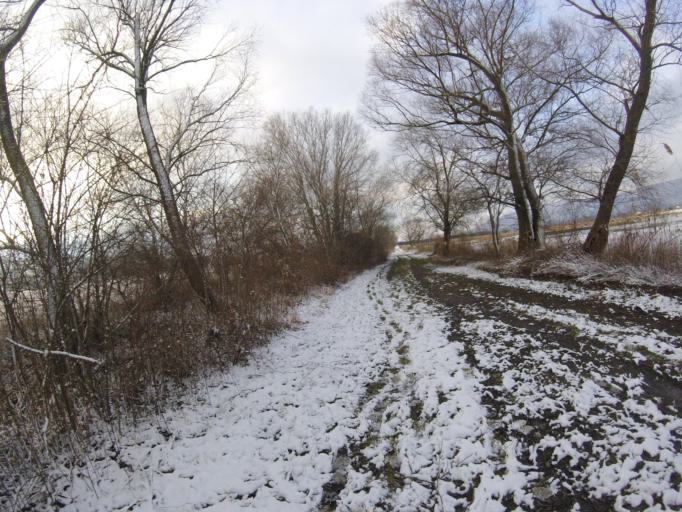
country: HU
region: Komarom-Esztergom
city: Esztergom
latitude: 47.8016
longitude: 18.7861
